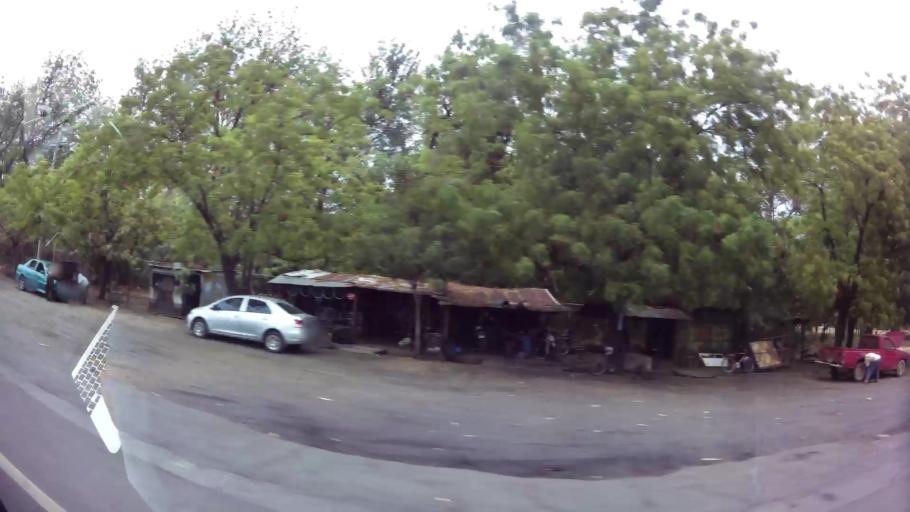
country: NI
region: Leon
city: Telica
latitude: 12.5225
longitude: -86.8702
